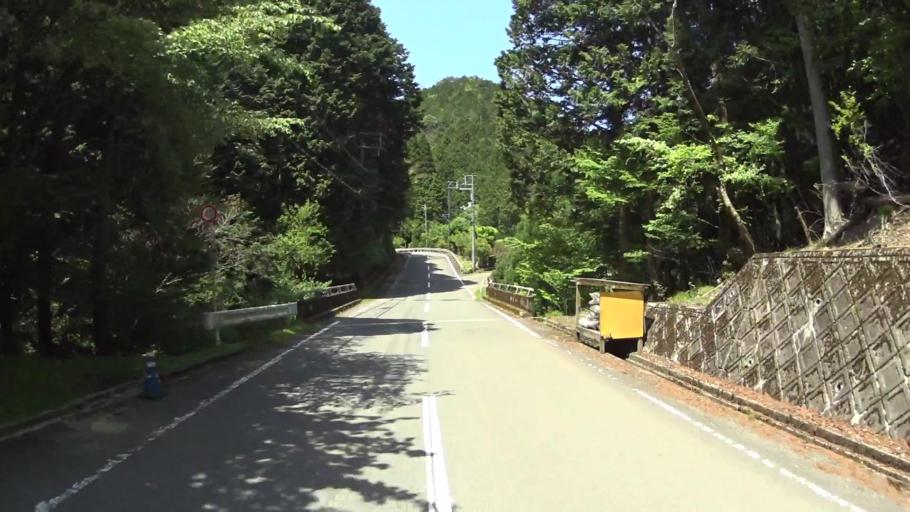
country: JP
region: Shiga Prefecture
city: Kitahama
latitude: 35.1522
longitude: 135.8322
